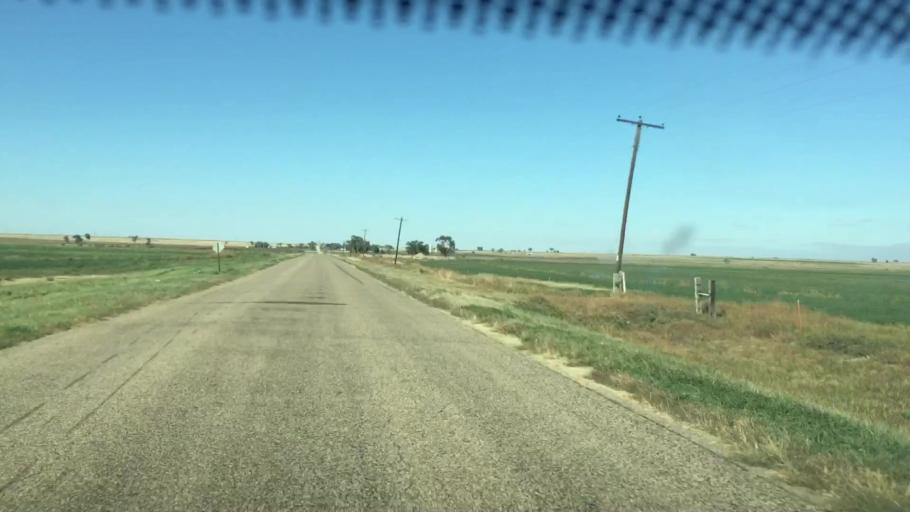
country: US
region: Colorado
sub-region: Prowers County
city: Lamar
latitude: 38.1030
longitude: -102.5215
